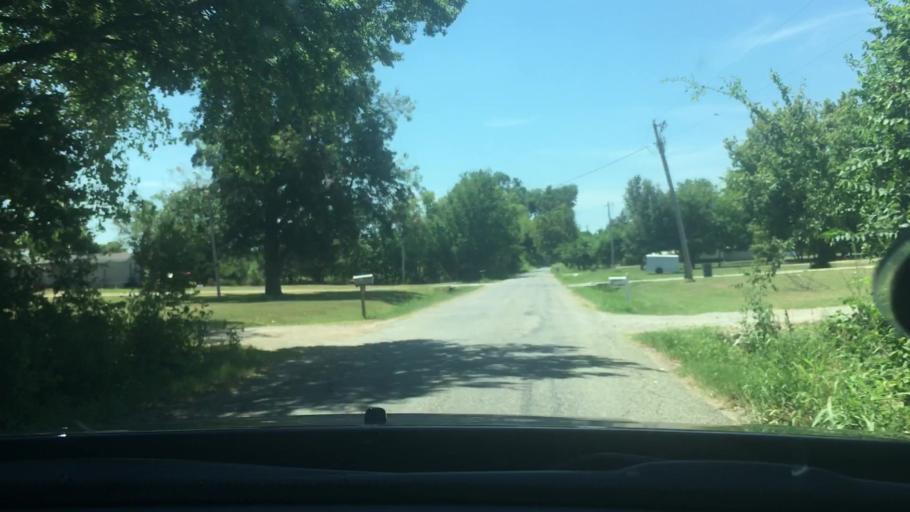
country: US
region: Oklahoma
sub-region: Bryan County
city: Durant
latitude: 33.9941
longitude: -96.2684
